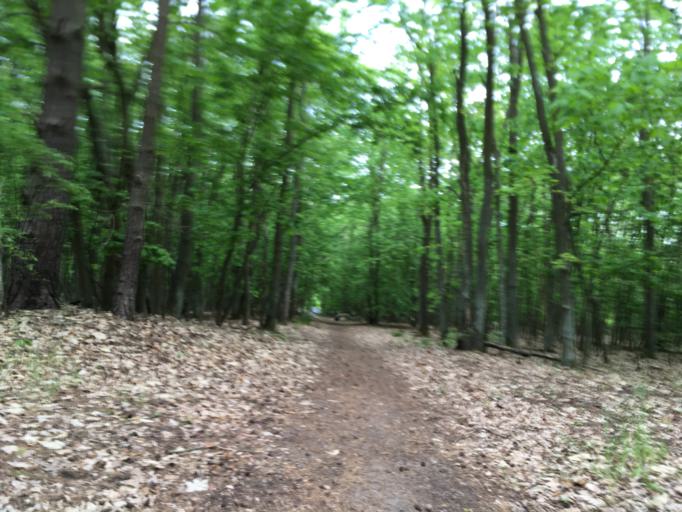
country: DE
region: Brandenburg
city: Marienwerder
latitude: 52.8479
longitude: 13.6103
